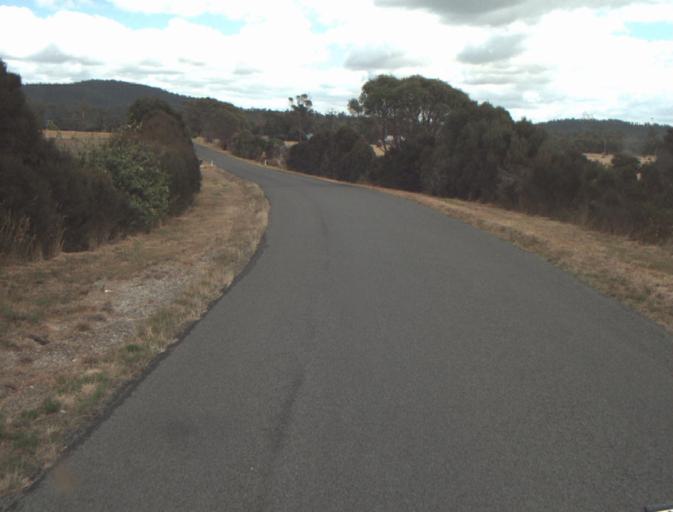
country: AU
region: Tasmania
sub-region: Launceston
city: Mayfield
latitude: -41.2065
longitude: 147.0618
